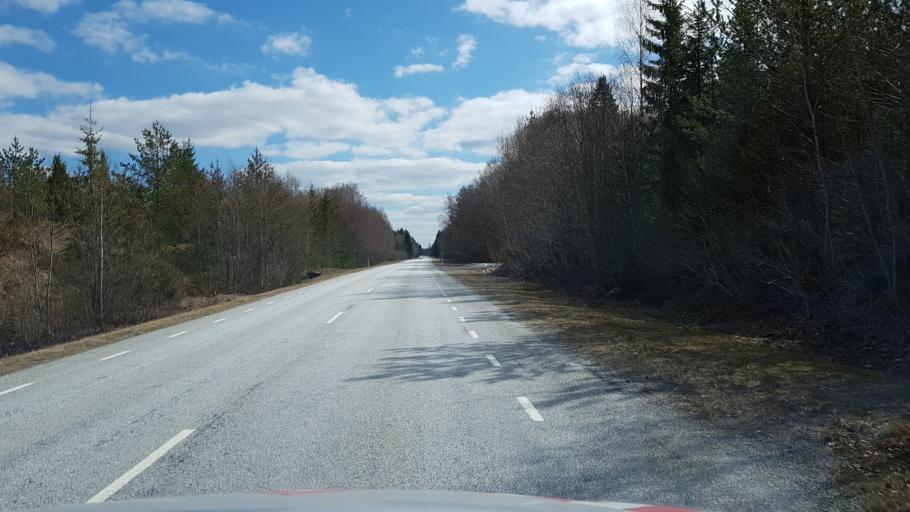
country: EE
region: Laeaene-Virumaa
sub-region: Rakke vald
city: Rakke
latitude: 58.9275
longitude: 26.2326
